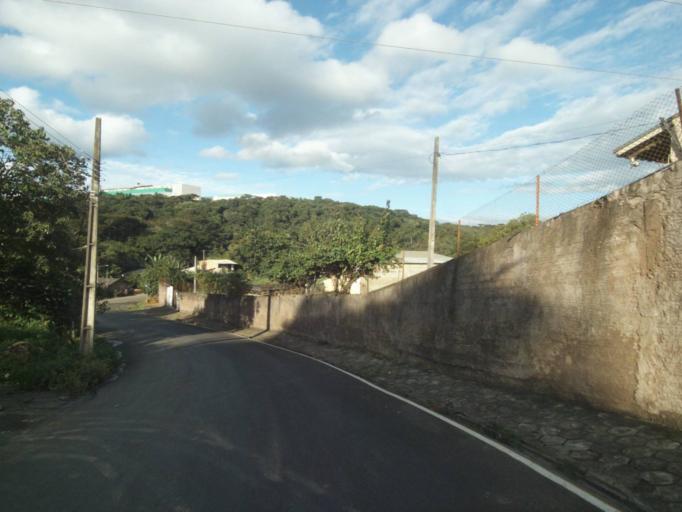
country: BR
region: Parana
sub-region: Telemaco Borba
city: Telemaco Borba
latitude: -24.3229
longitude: -50.6118
